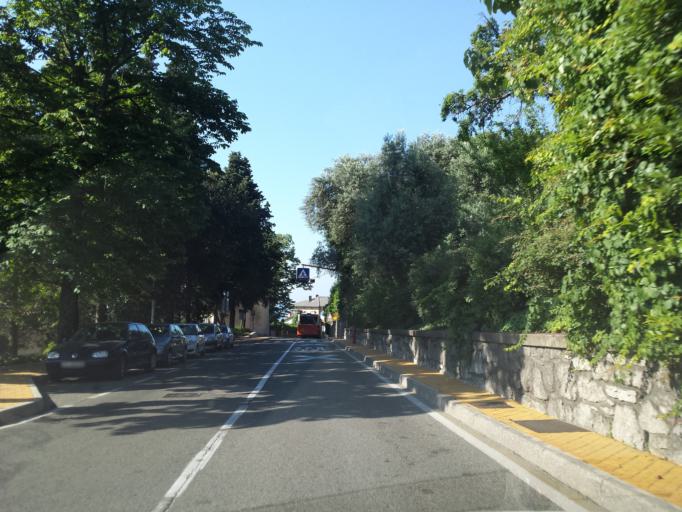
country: HR
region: Primorsko-Goranska
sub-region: Grad Opatija
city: Opatija
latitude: 45.3478
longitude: 14.3183
